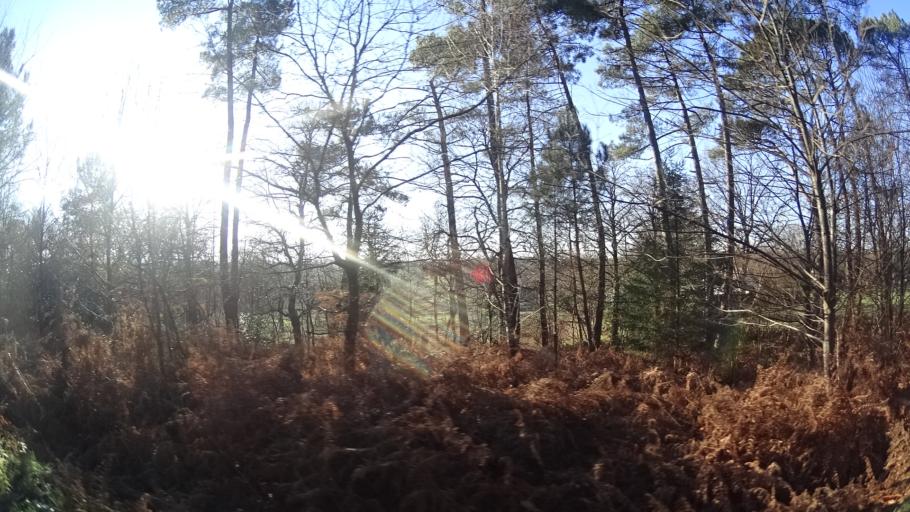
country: FR
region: Brittany
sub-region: Departement du Morbihan
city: Allaire
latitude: 47.6626
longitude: -2.1793
